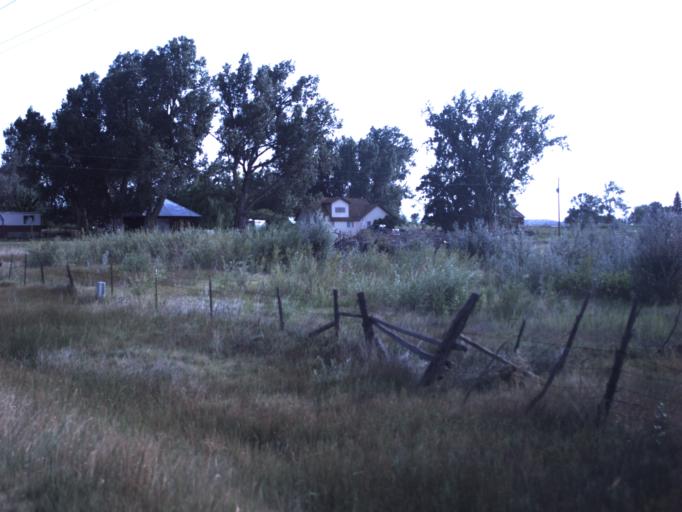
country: US
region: Utah
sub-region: Duchesne County
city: Duchesne
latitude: 40.3470
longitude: -110.2752
